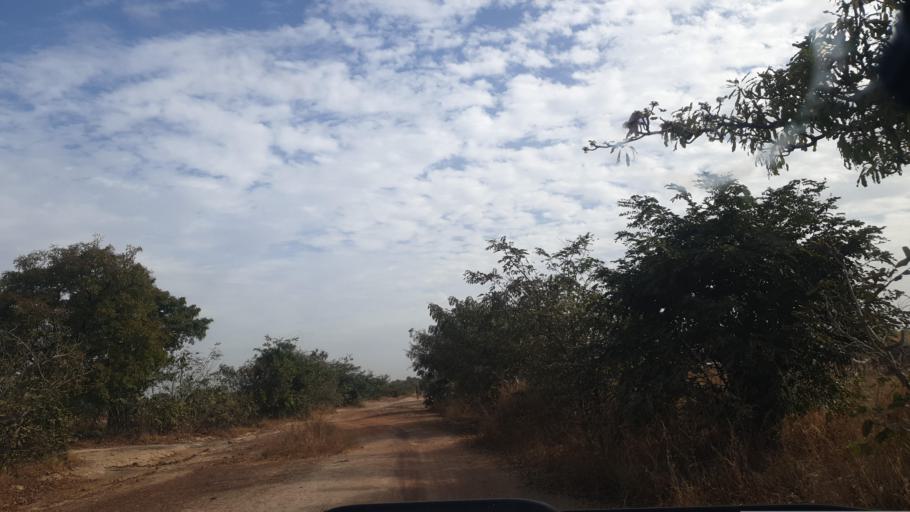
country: ML
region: Sikasso
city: Yanfolila
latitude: 11.4116
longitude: -8.0056
